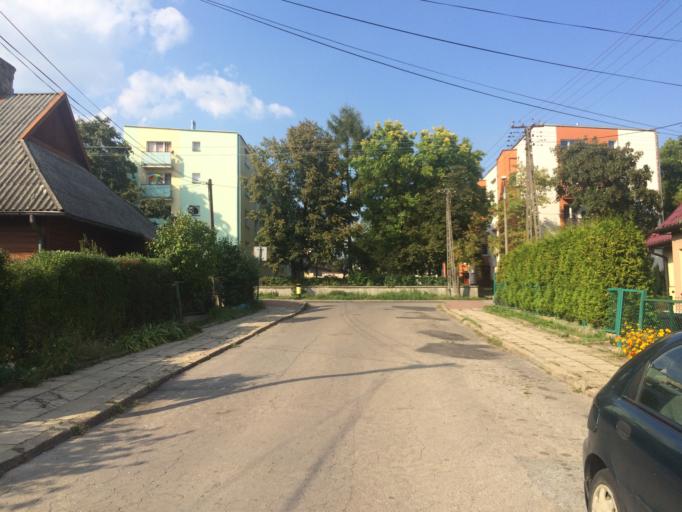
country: PL
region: Swietokrzyskie
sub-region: Powiat starachowicki
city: Starachowice
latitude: 51.0565
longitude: 21.0687
